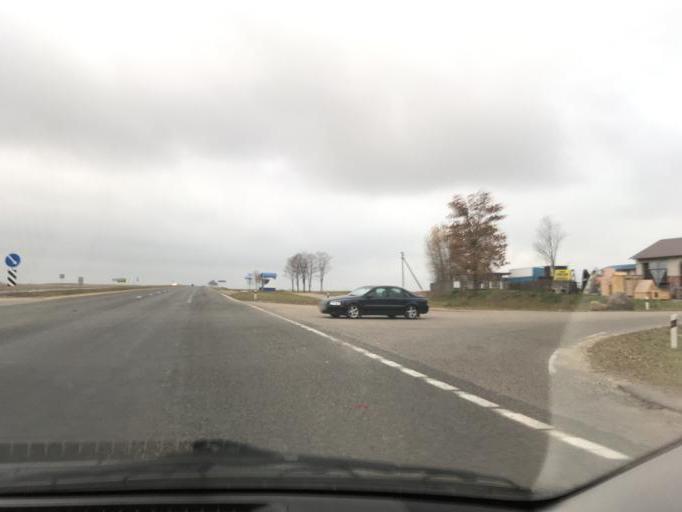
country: BY
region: Vitebsk
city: Vitebsk
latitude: 55.1518
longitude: 30.1107
